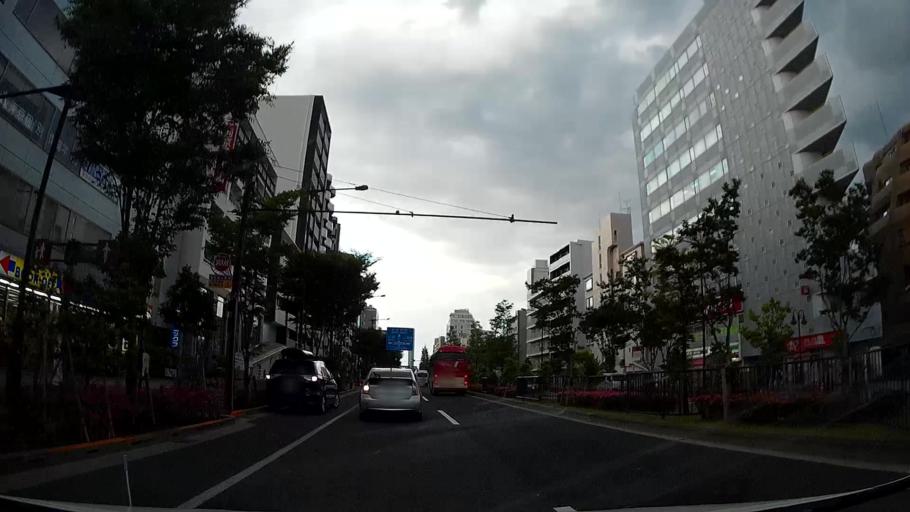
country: JP
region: Tokyo
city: Tokyo
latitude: 35.7076
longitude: 139.6833
